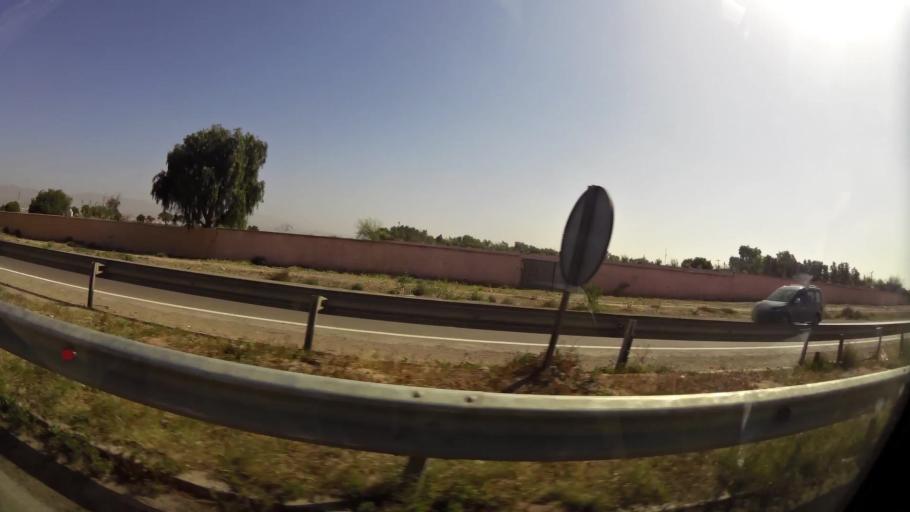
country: MA
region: Souss-Massa-Draa
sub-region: Inezgane-Ait Mellou
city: Inezgane
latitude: 30.3584
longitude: -9.4889
